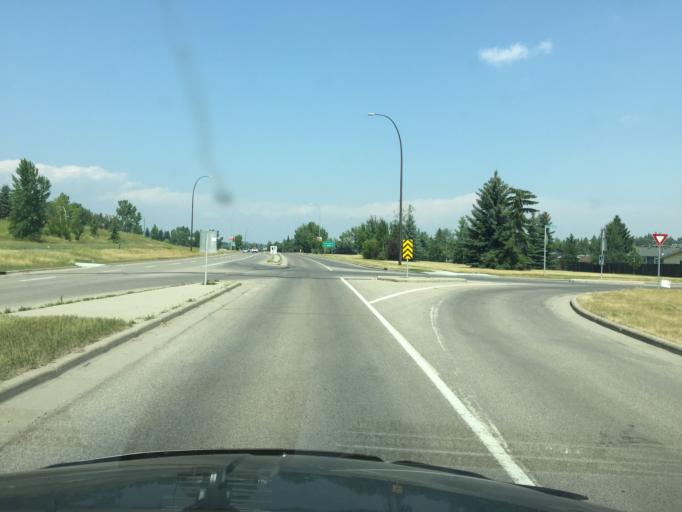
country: CA
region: Alberta
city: Calgary
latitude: 50.9163
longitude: -114.0169
